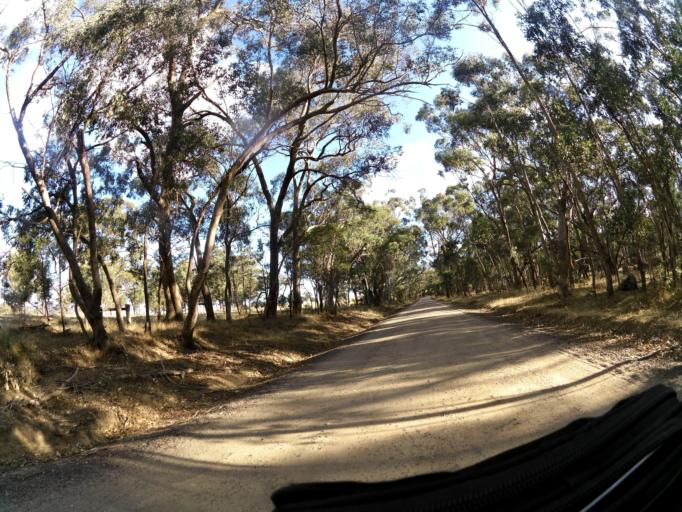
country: AU
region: Victoria
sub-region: Greater Bendigo
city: Kennington
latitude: -37.0185
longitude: 144.8061
